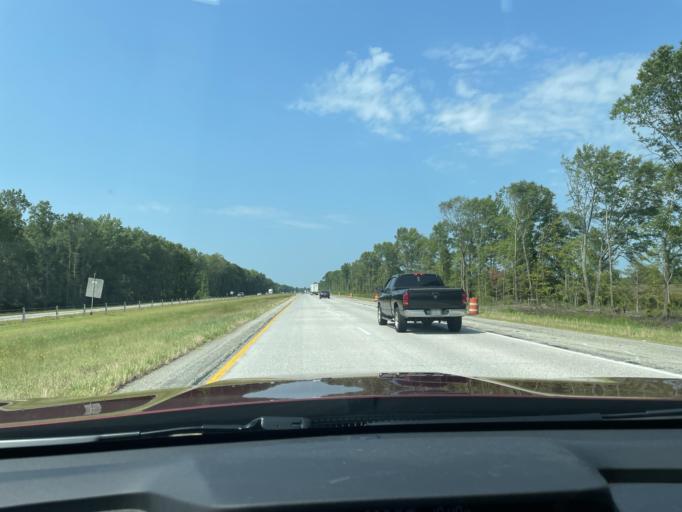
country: US
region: Arkansas
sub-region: White County
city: Searcy
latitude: 35.1624
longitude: -91.7794
